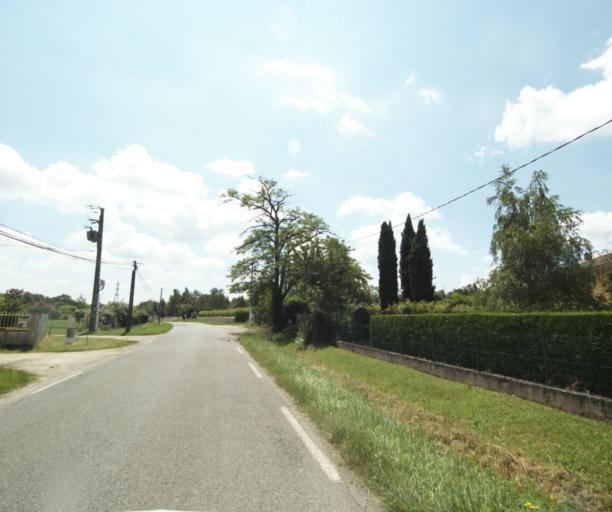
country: FR
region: Midi-Pyrenees
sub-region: Departement du Tarn-et-Garonne
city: Montauban
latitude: 44.0571
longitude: 1.3380
